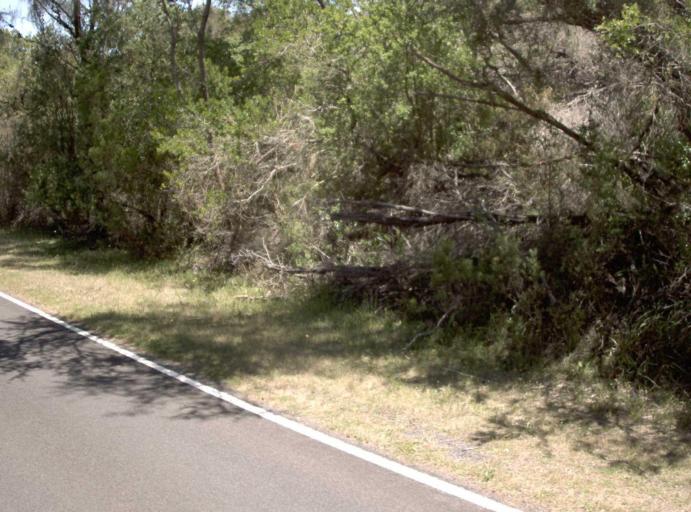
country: AU
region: Victoria
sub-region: Latrobe
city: Morwell
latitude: -38.8760
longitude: 146.2668
